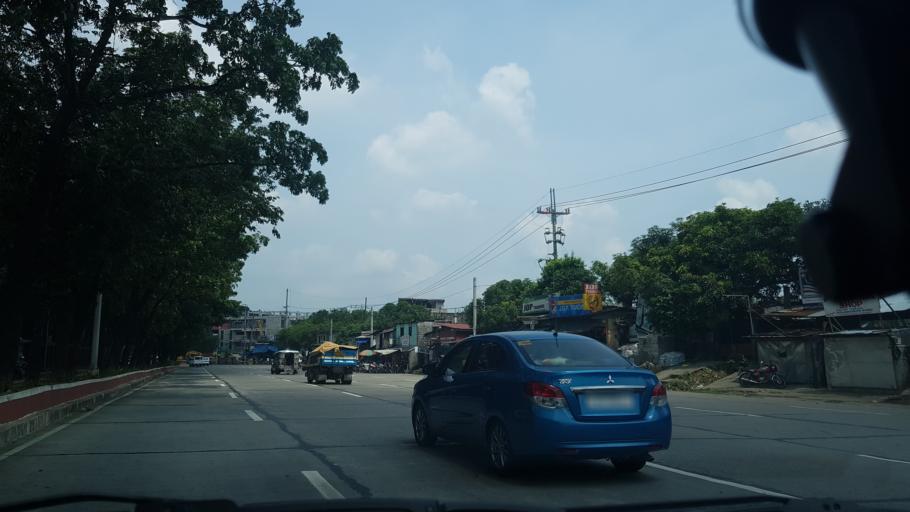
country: PH
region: Calabarzon
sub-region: Province of Rizal
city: San Mateo
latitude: 14.6934
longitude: 121.0964
